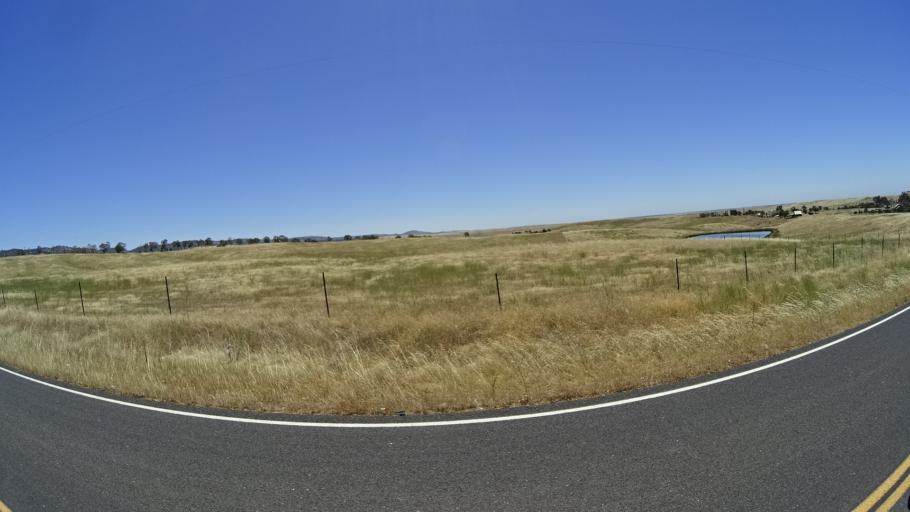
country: US
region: California
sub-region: Calaveras County
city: Rancho Calaveras
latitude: 38.0386
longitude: -120.8489
